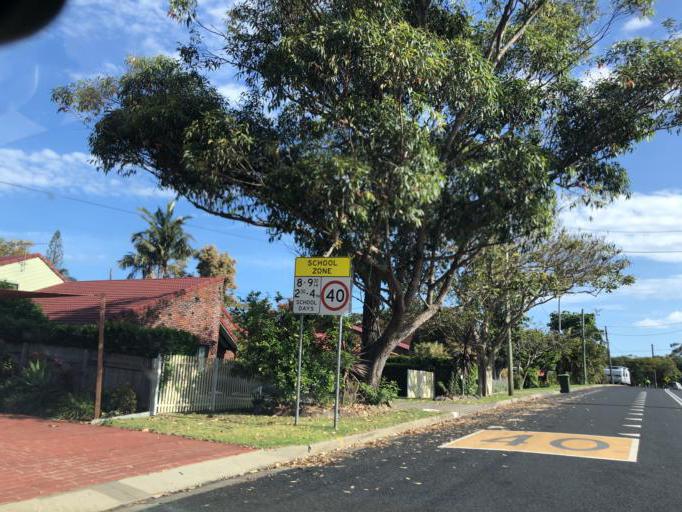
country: AU
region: New South Wales
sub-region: Coffs Harbour
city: Coffs Harbour
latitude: -30.2527
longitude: 153.1339
